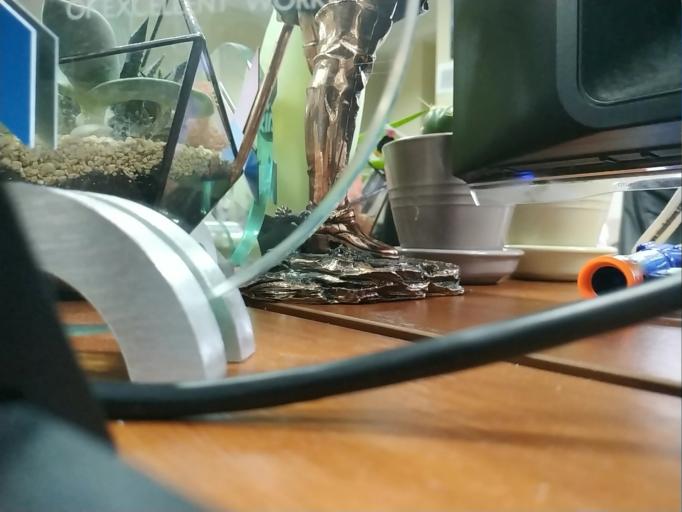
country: RU
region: Moskovskaya
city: Lugovaya
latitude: 56.0775
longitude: 37.4619
